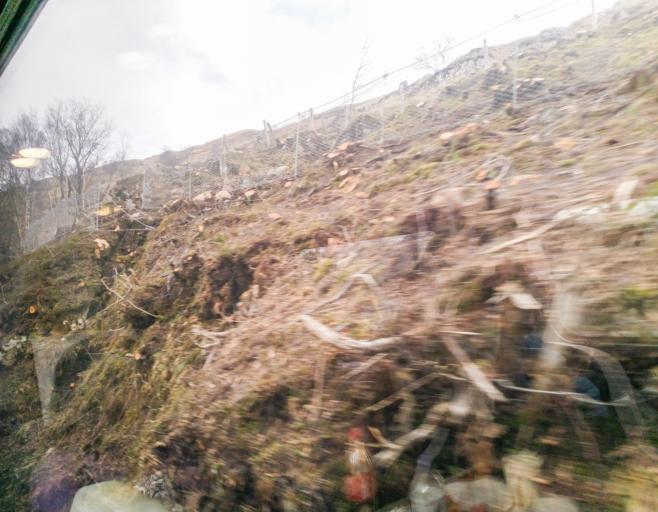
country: GB
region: Scotland
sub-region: Highland
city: Spean Bridge
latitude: 56.7866
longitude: -4.7305
